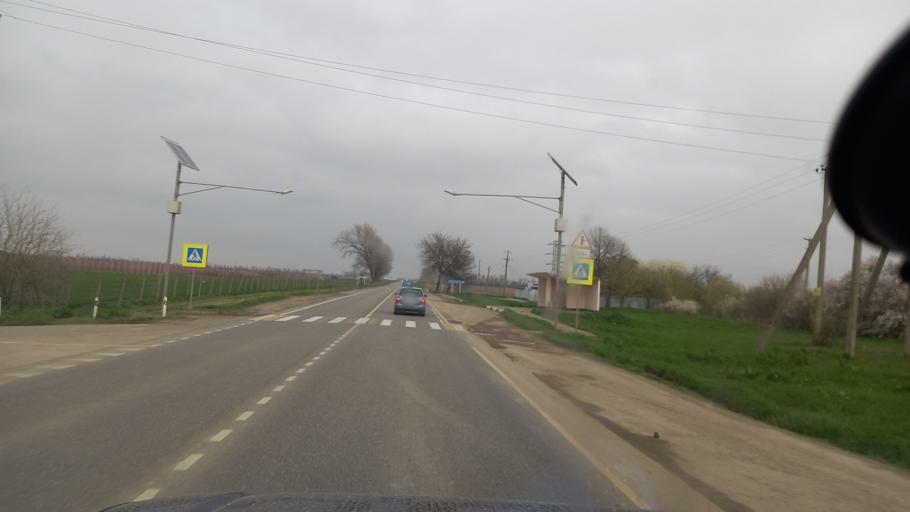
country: RU
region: Krasnodarskiy
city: Slavyansk-na-Kubani
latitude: 45.2432
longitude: 38.0381
